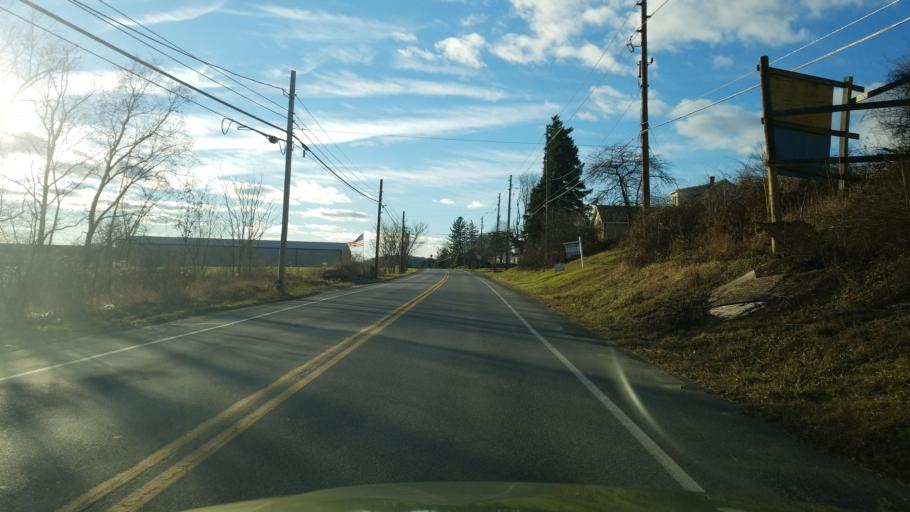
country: US
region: Pennsylvania
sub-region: Indiana County
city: Indiana
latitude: 40.6233
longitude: -79.1820
